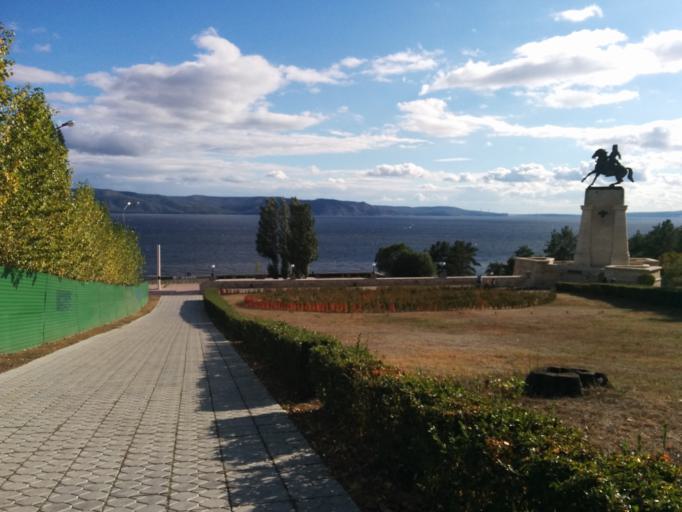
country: RU
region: Samara
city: Tol'yatti
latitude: 53.4752
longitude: 49.3493
